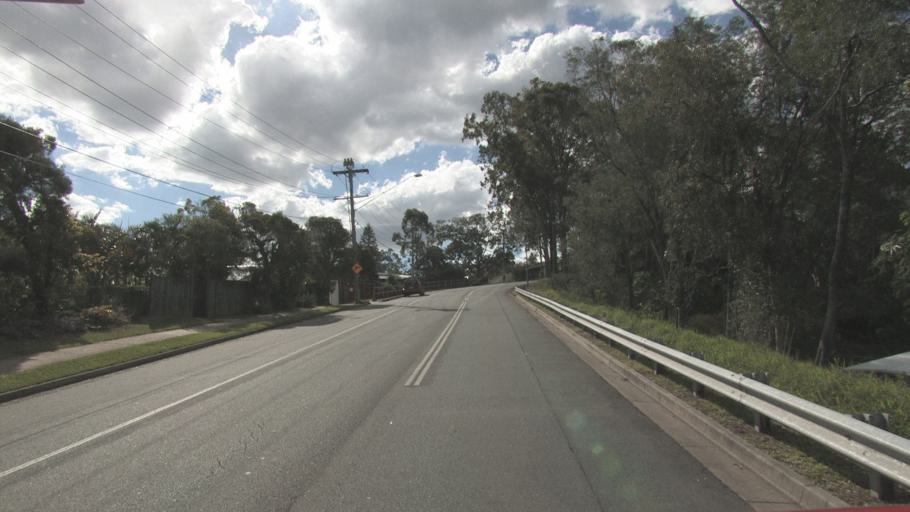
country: AU
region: Queensland
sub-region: Logan
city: Slacks Creek
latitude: -27.6309
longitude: 153.1548
